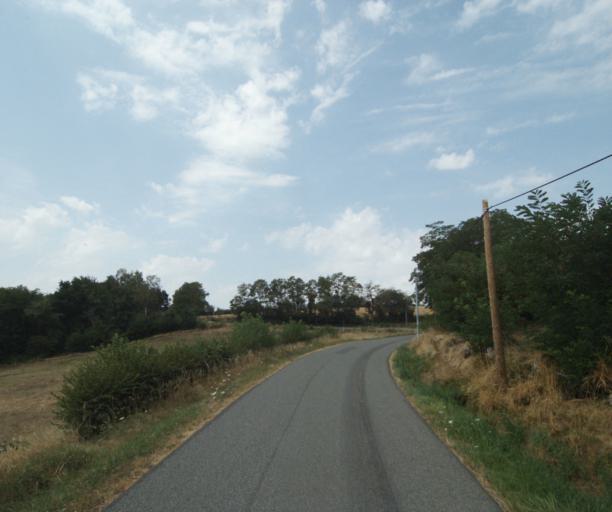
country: FR
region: Bourgogne
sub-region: Departement de Saone-et-Loire
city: Gueugnon
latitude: 46.6036
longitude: 4.0067
